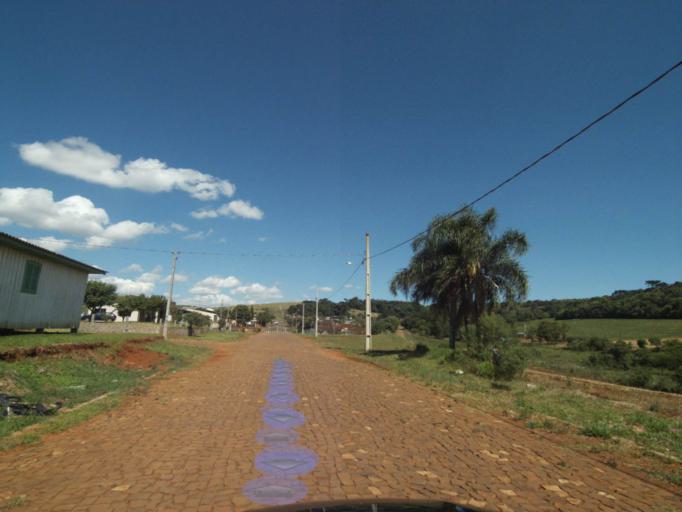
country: BR
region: Parana
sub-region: Coronel Vivida
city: Coronel Vivida
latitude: -26.1467
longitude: -52.3863
